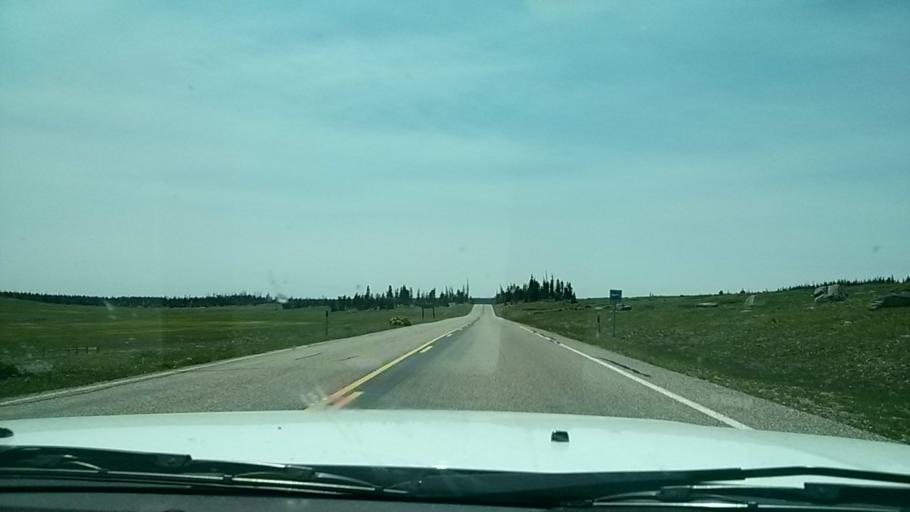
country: US
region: Utah
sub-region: Iron County
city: Cedar City
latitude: 37.6046
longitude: -112.8509
